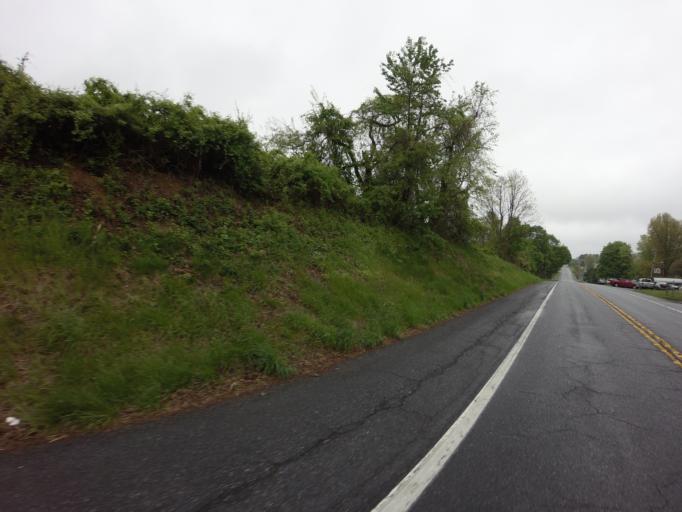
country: US
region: Maryland
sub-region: Frederick County
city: Myersville
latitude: 39.4928
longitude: -77.5373
